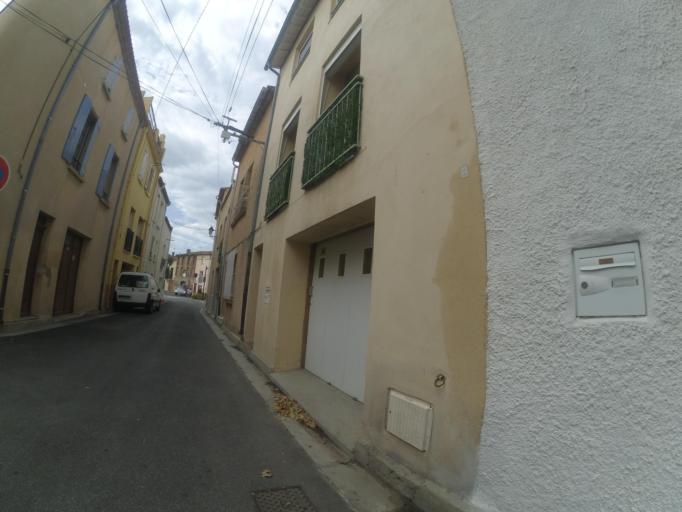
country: FR
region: Languedoc-Roussillon
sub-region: Departement des Pyrenees-Orientales
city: Toulouges
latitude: 42.6706
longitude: 2.8308
